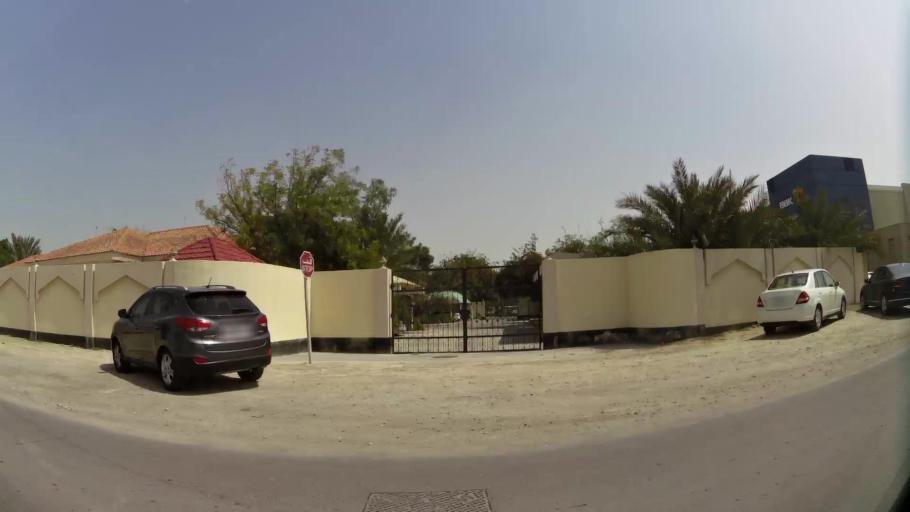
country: BH
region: Manama
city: Jidd Hafs
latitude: 26.2189
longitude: 50.4859
